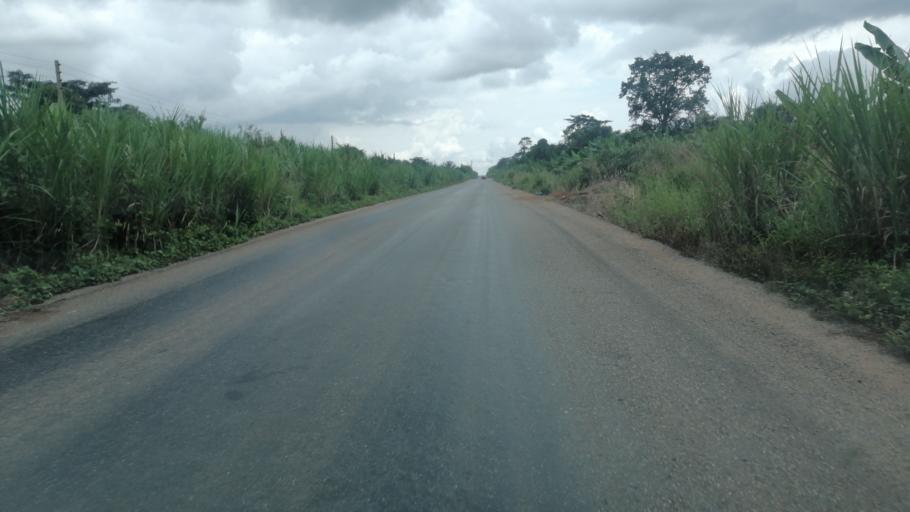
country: GH
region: Western
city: Bibiani
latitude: 6.8719
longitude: -2.4353
